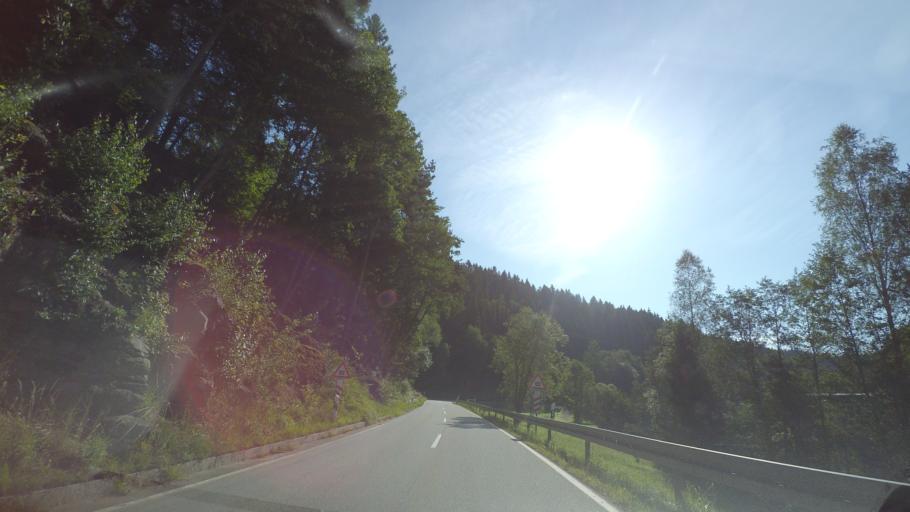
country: DE
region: Bavaria
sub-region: Lower Bavaria
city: Geiersthal
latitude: 49.0735
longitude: 12.9980
